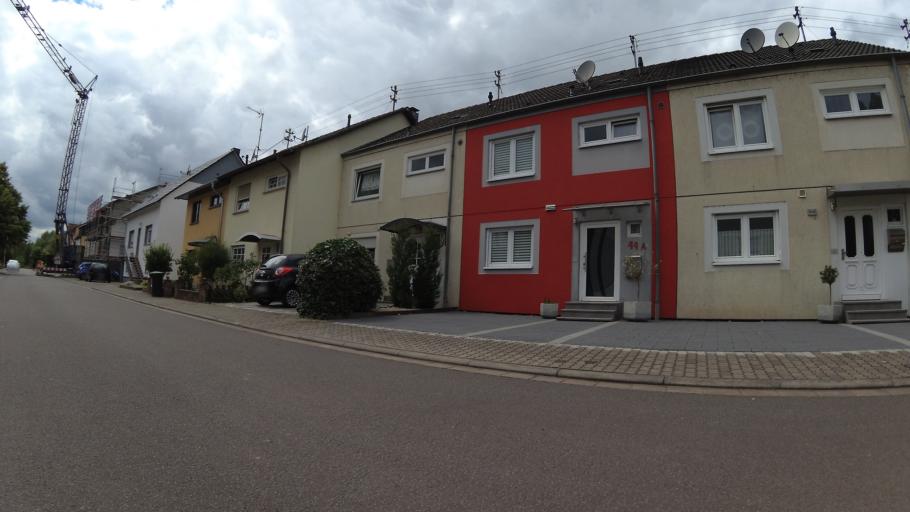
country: DE
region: Saarland
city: Nalbach
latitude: 49.3735
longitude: 6.7862
